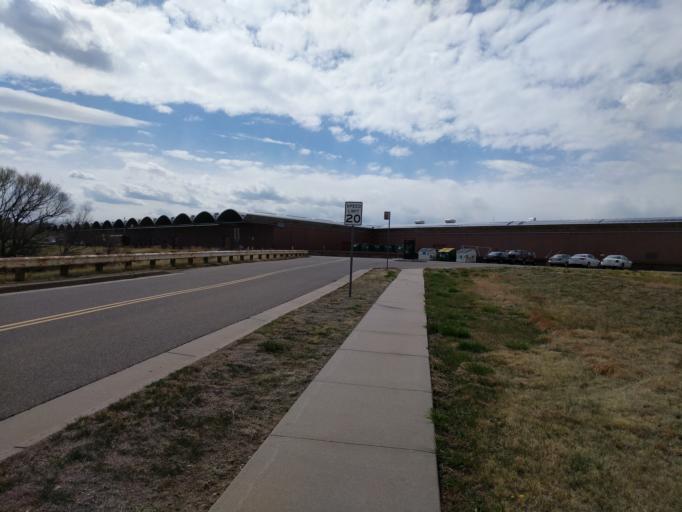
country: US
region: Colorado
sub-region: Jefferson County
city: Lakewood
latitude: 39.7143
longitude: -105.1224
